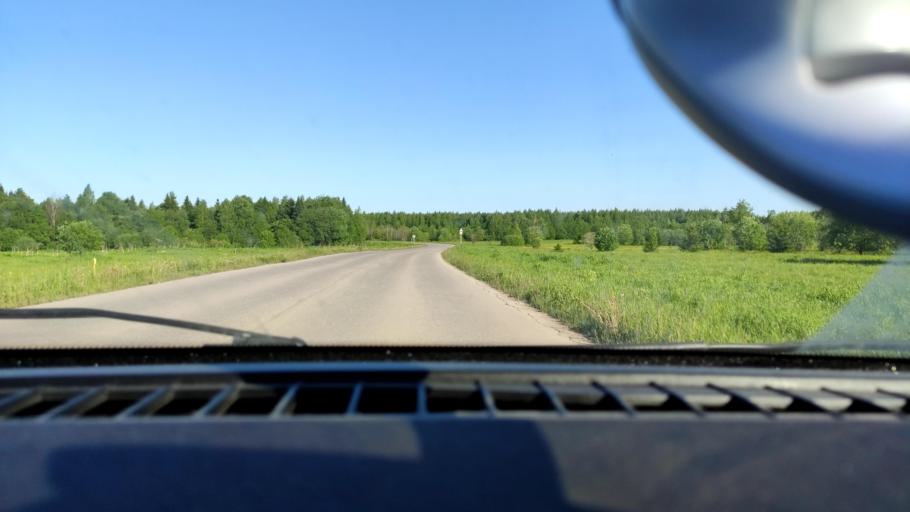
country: RU
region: Perm
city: Polazna
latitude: 58.2133
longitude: 56.4309
